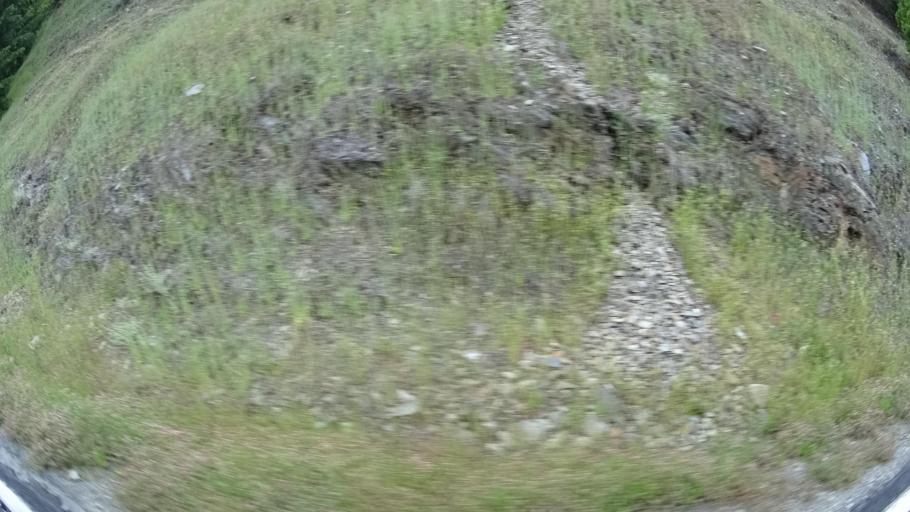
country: US
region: California
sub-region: Humboldt County
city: Willow Creek
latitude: 41.2560
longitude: -123.6297
